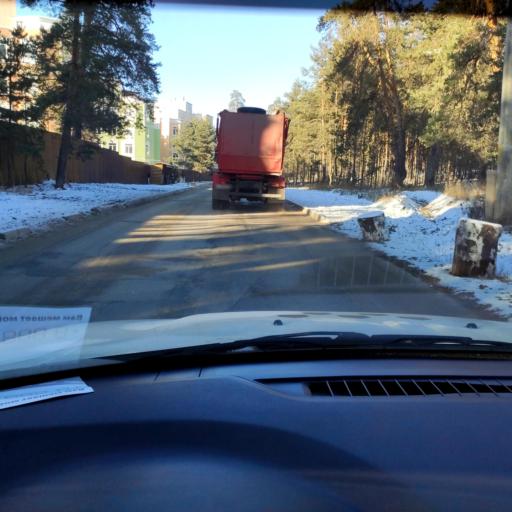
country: RU
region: Samara
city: Tol'yatti
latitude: 53.4690
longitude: 49.3733
